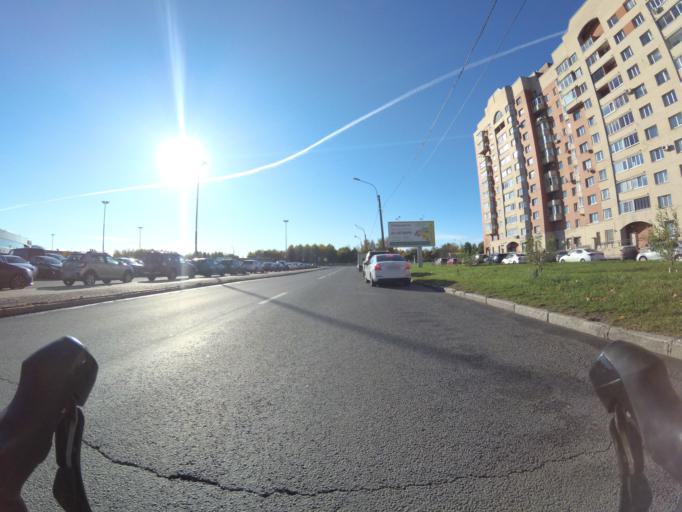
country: RU
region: Leningrad
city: Untolovo
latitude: 59.9860
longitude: 30.2014
